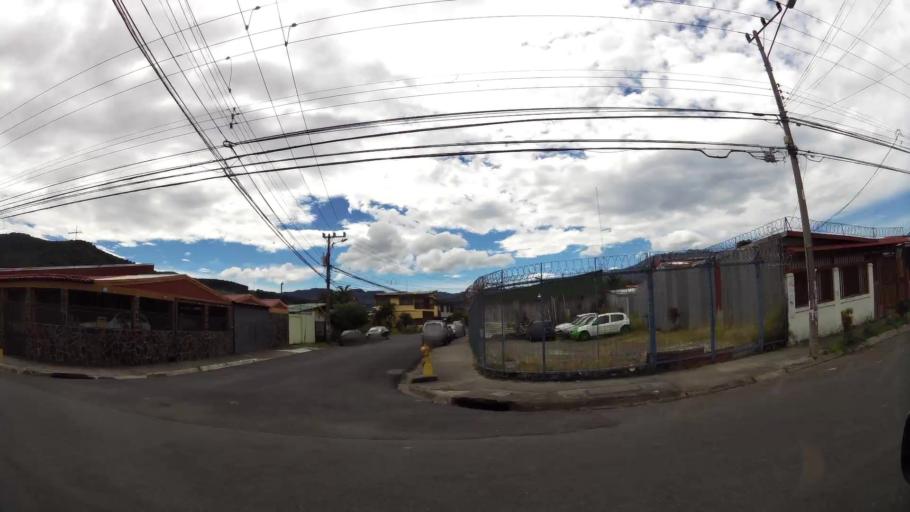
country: CR
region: San Jose
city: San Miguel
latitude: 9.8939
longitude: -84.0554
